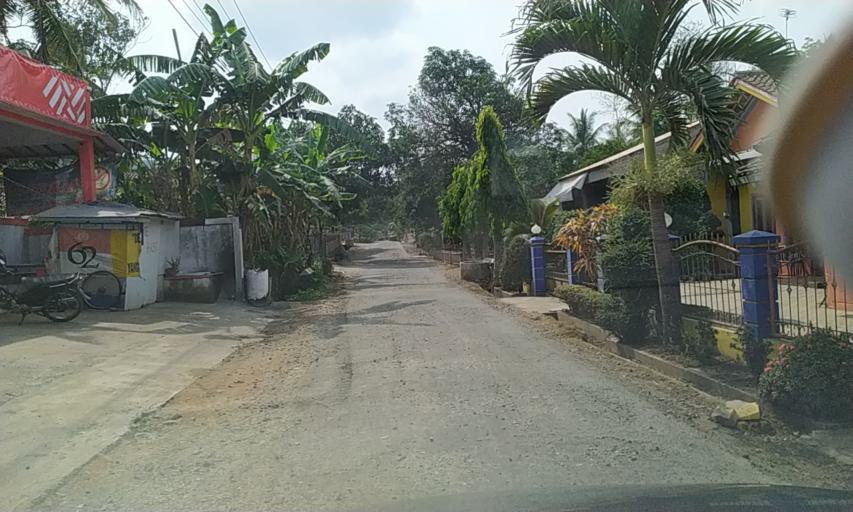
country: ID
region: Central Java
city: Cibatu
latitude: -7.4084
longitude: 108.7596
